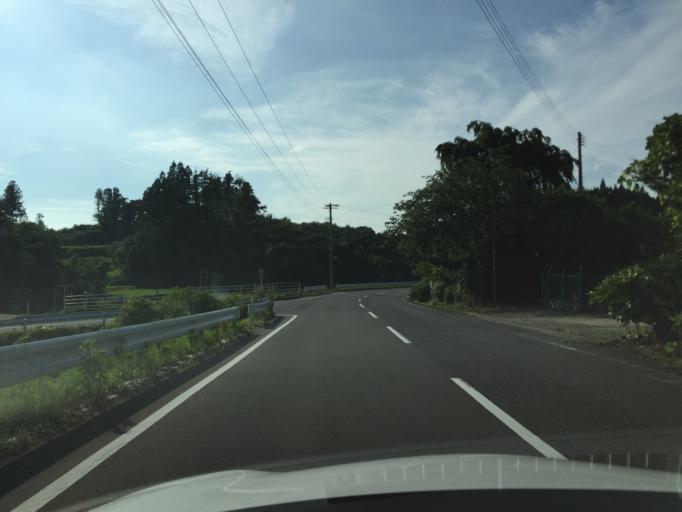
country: JP
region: Fukushima
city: Miharu
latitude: 37.3680
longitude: 140.5140
